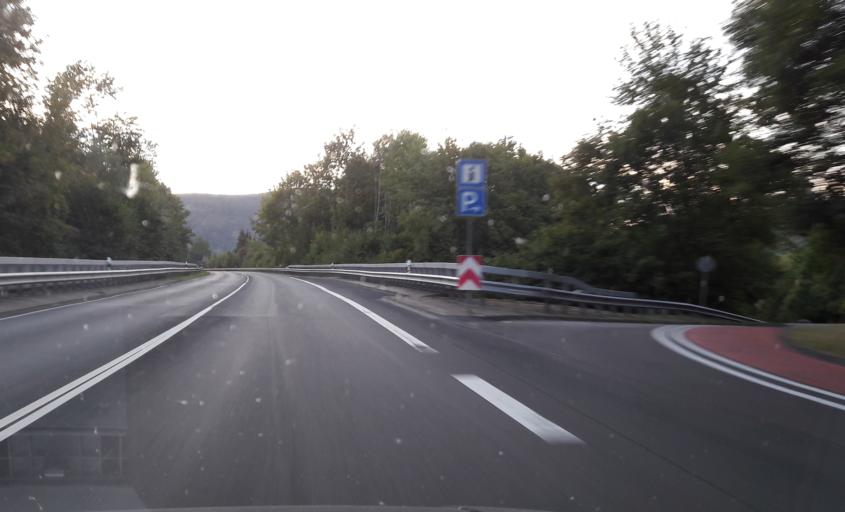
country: DE
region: Rheinland-Pfalz
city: Punderich
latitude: 50.0364
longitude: 7.1382
